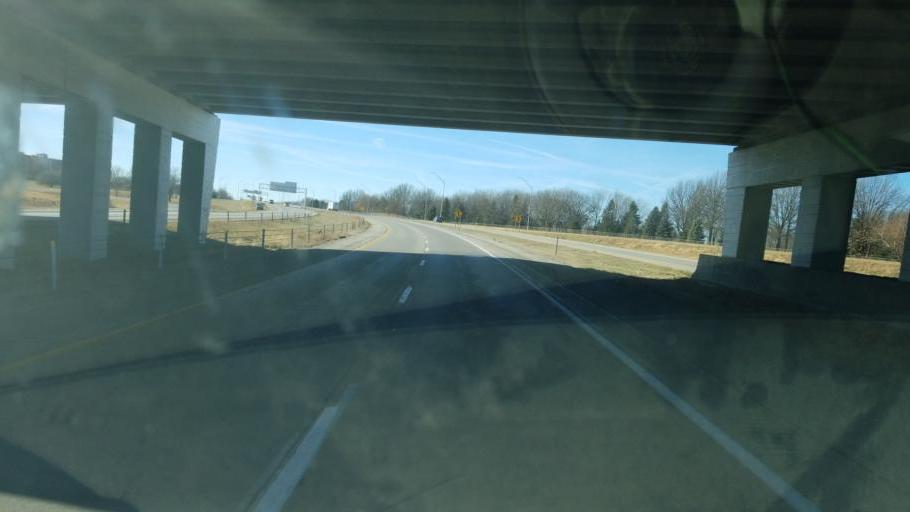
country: US
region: Iowa
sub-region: Dallas County
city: Waukee
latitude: 41.5919
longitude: -93.8088
